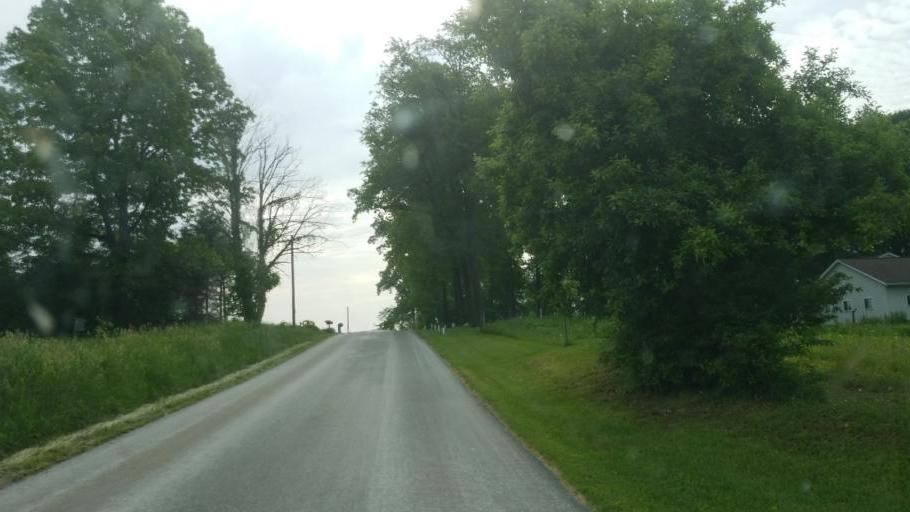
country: US
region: Ohio
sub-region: Wayne County
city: Apple Creek
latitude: 40.6824
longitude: -81.7561
